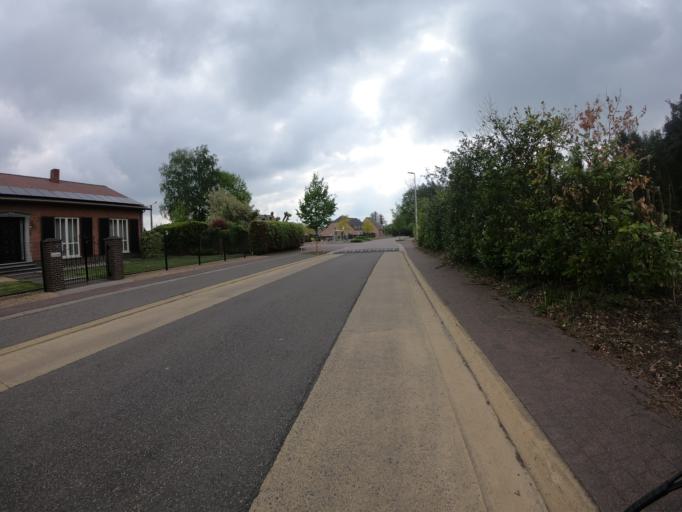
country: BE
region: Flanders
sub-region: Provincie Limburg
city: Genk
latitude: 50.9249
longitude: 5.4760
